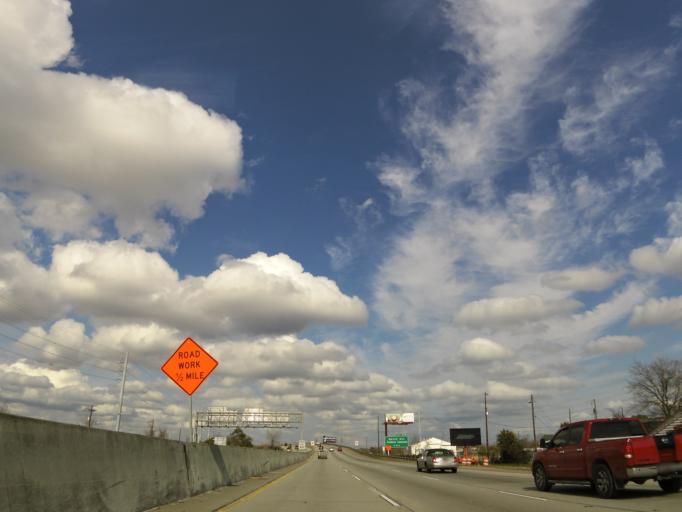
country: US
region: South Carolina
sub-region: Charleston County
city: North Charleston
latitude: 32.8205
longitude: -79.9545
